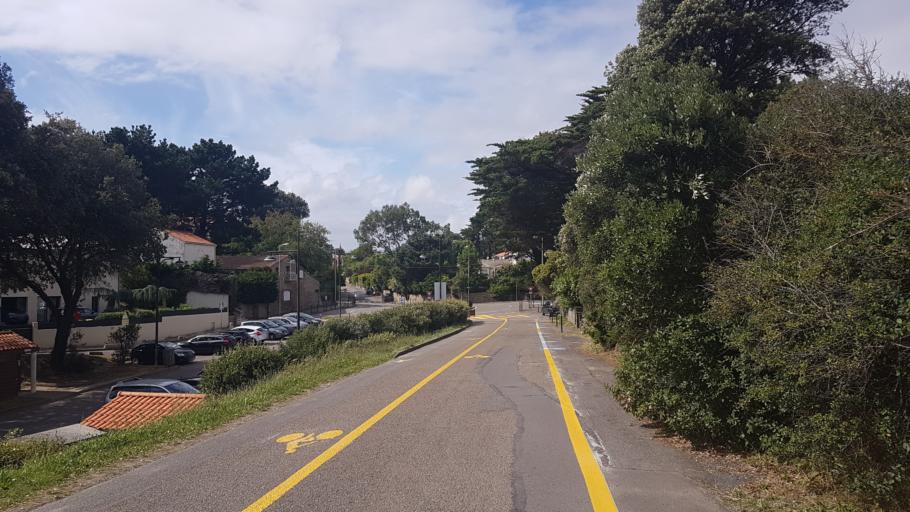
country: FR
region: Pays de la Loire
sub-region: Departement de la Loire-Atlantique
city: La Plaine-sur-Mer
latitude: 47.1141
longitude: -2.1465
